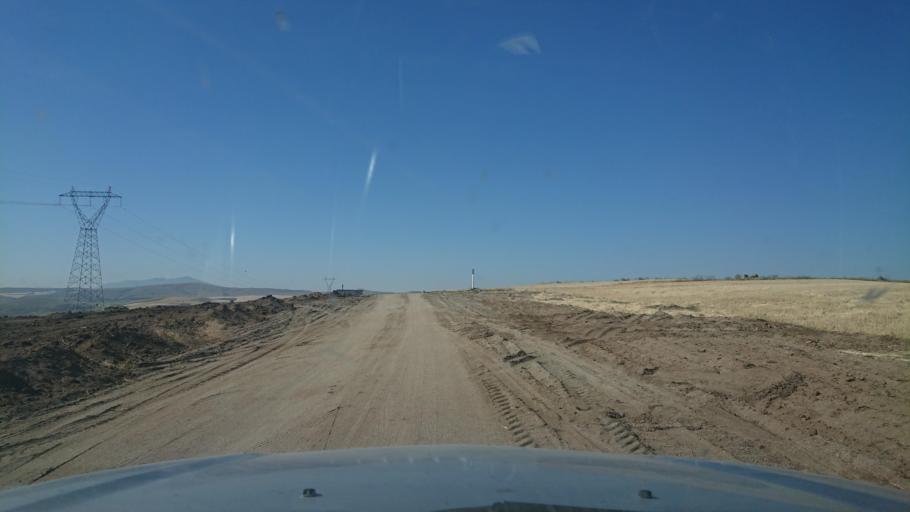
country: TR
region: Aksaray
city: Agacoren
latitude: 38.8421
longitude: 33.9441
